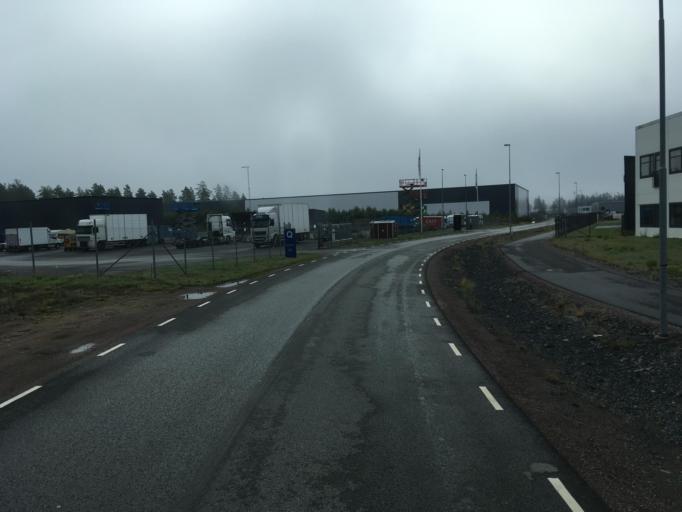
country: SE
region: Joenkoeping
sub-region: Jonkopings Kommun
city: Jonkoping
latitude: 57.7680
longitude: 14.0840
